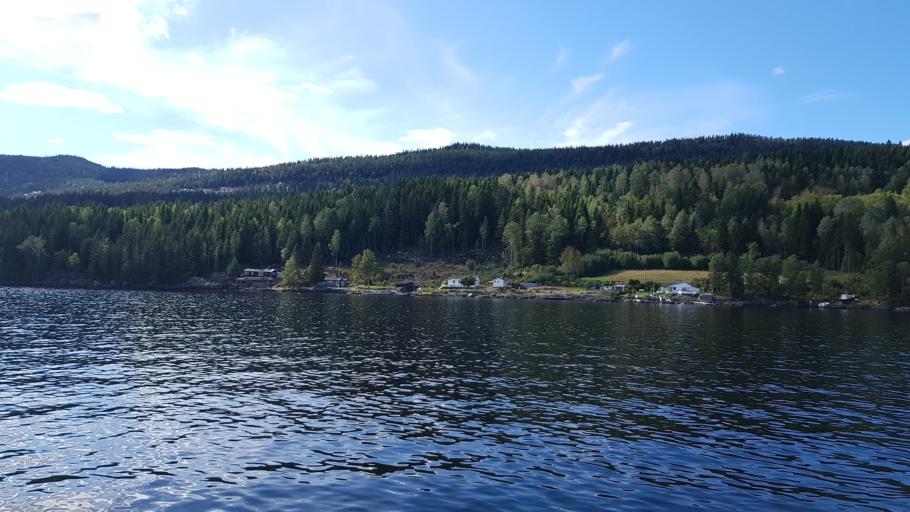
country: NO
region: Akershus
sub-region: Hurdal
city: Hurdal
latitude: 60.5440
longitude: 11.1986
